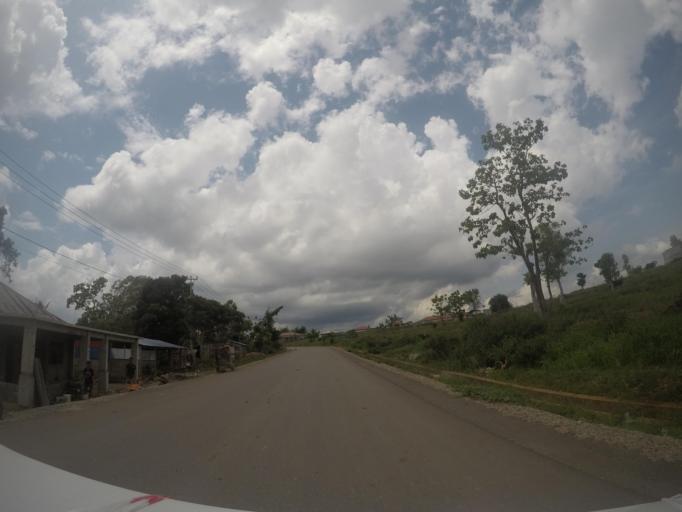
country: TL
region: Baucau
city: Venilale
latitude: -8.5647
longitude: 126.3980
